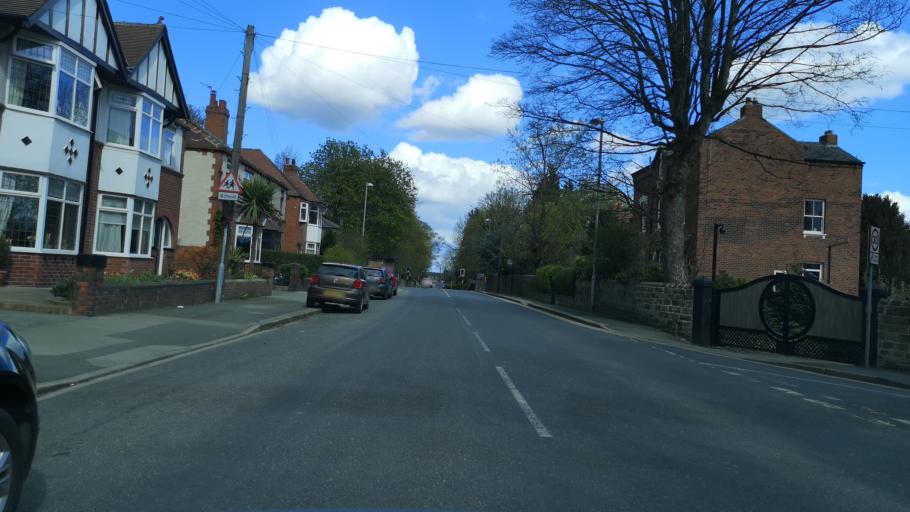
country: GB
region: England
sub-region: City and Borough of Wakefield
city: Horbury
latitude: 53.6604
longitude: -1.5507
